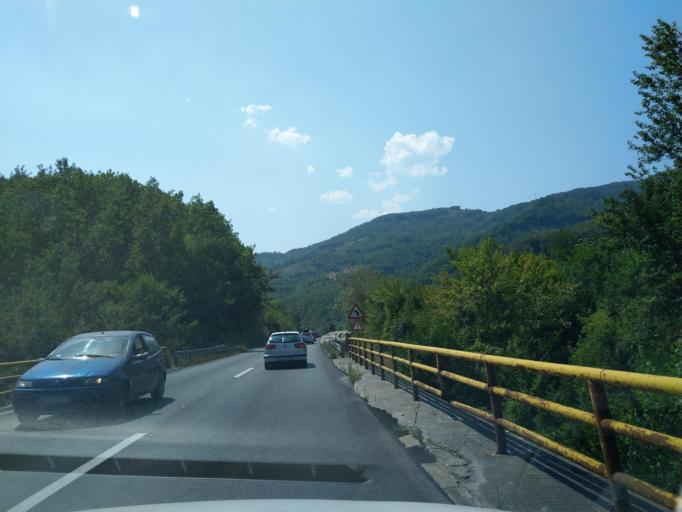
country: RS
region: Central Serbia
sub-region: Zlatiborski Okrug
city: Prijepolje
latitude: 43.4473
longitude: 19.6387
